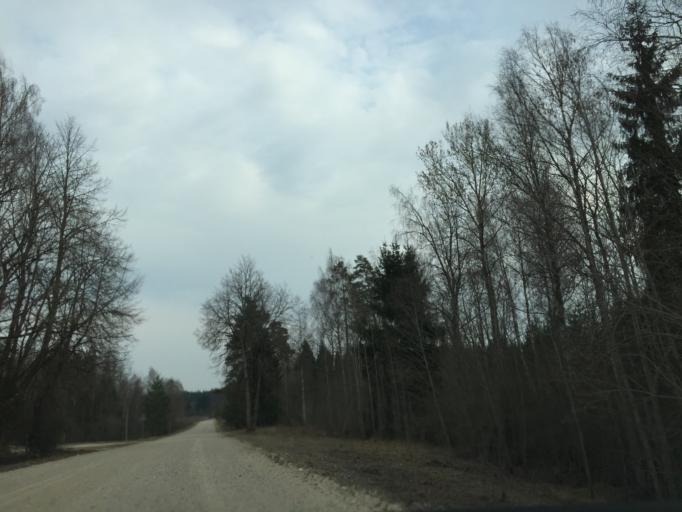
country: LV
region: Priekuli
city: Priekuli
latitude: 57.2082
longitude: 25.4263
